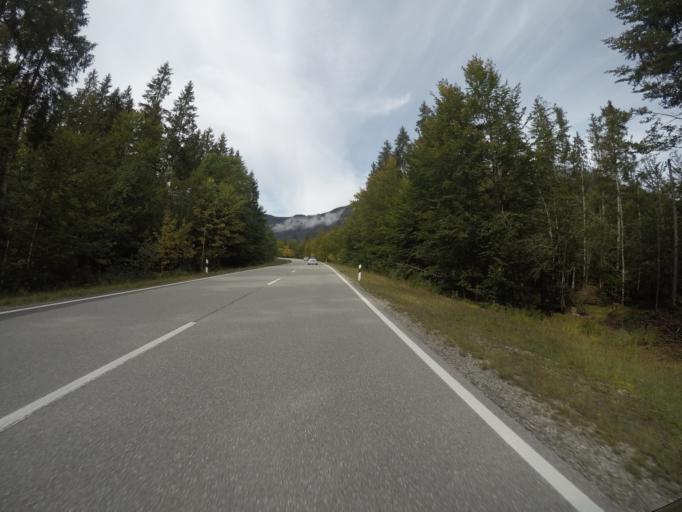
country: DE
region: Bavaria
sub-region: Upper Bavaria
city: Jachenau
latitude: 47.5589
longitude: 11.4733
